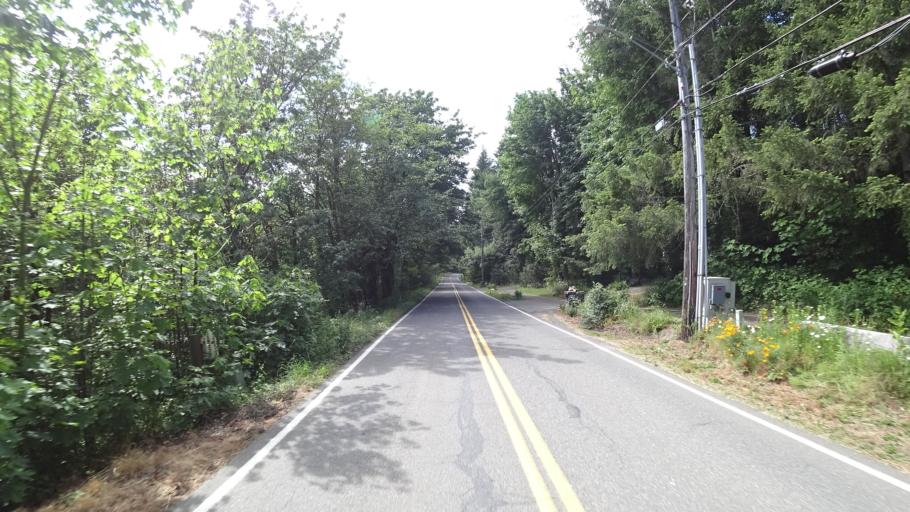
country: US
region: Oregon
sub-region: Washington County
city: Oak Hills
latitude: 45.5894
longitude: -122.8102
